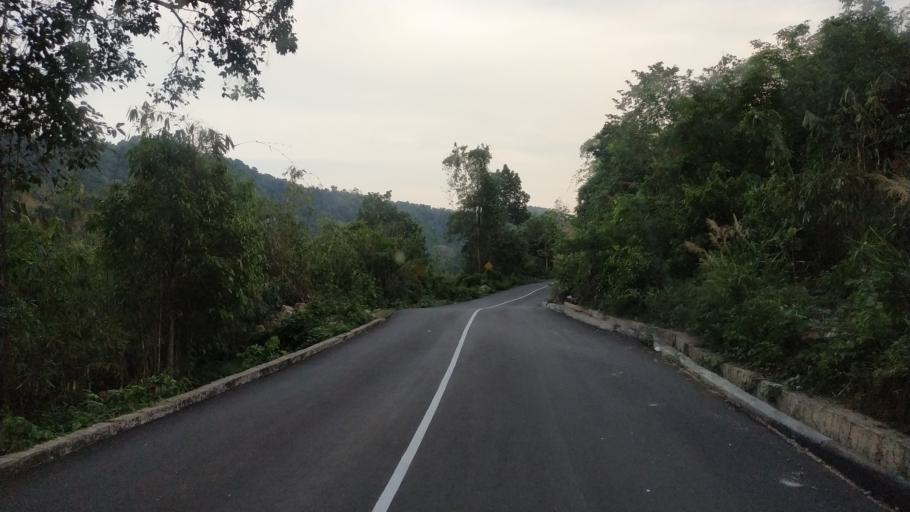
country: MM
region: Mon
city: Kyaikto
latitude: 17.4421
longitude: 97.0981
